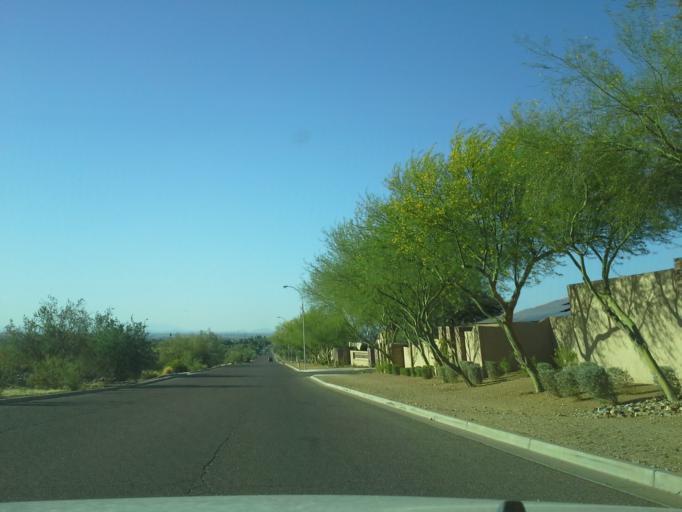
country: US
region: Arizona
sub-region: Maricopa County
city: Laveen
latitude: 33.3561
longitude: -112.1005
